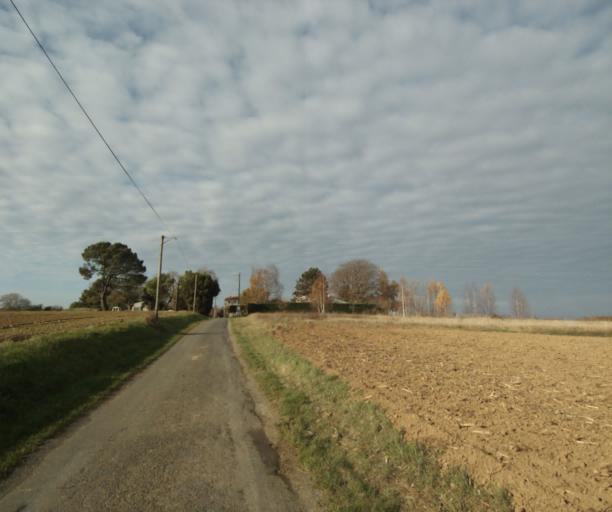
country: FR
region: Poitou-Charentes
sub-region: Departement de la Charente-Maritime
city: Corme-Royal
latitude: 45.7309
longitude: -0.8111
